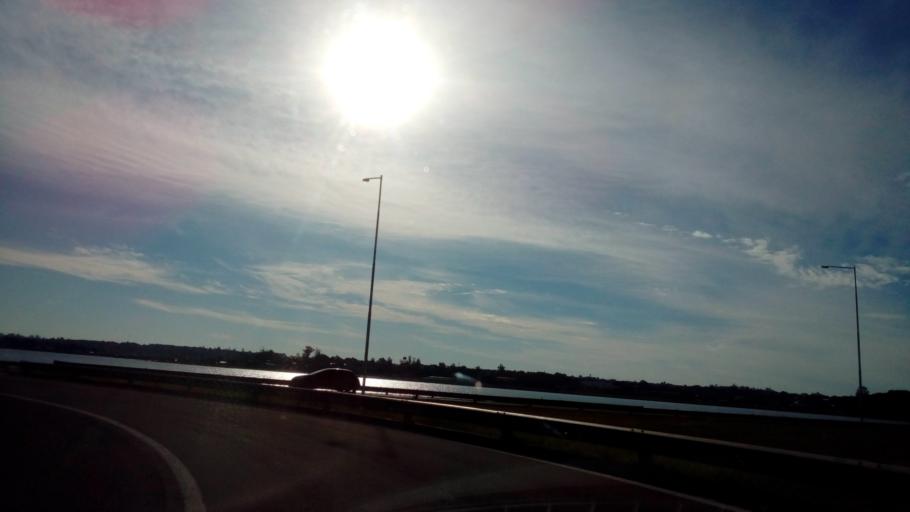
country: AR
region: Misiones
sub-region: Departamento de Capital
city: Posadas
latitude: -27.4126
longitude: -55.8885
